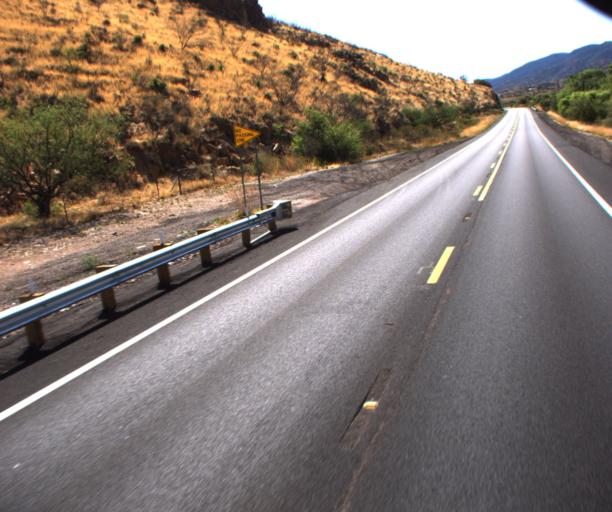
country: US
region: Arizona
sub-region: Cochise County
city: Bisbee
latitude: 31.5017
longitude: -110.0050
